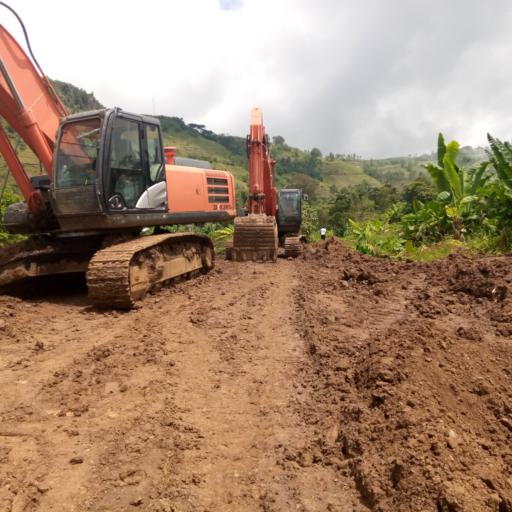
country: ET
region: Southern Nations, Nationalities, and People's Region
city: Arba Minch'
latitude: 6.3163
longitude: 37.3596
